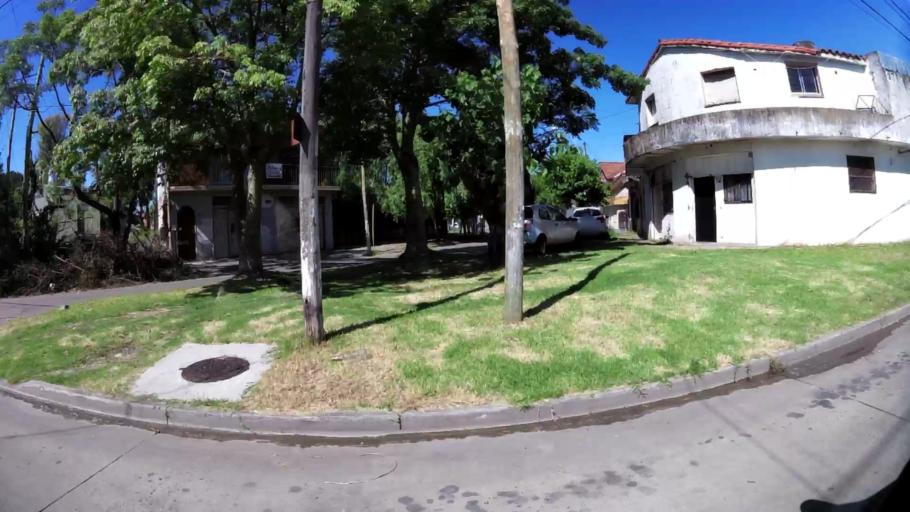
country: AR
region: Buenos Aires
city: Ituzaingo
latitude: -34.6260
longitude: -58.6556
